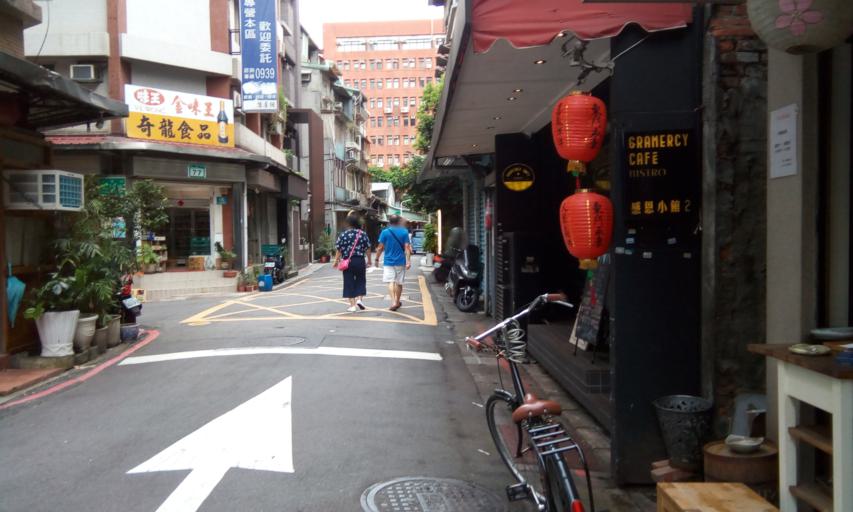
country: TW
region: Taipei
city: Taipei
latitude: 25.0292
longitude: 121.5297
